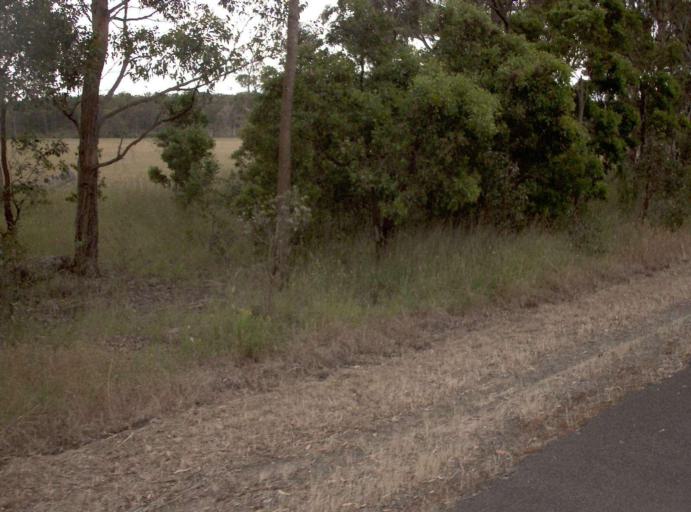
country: AU
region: Victoria
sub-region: Wellington
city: Sale
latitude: -38.4690
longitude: 146.9301
